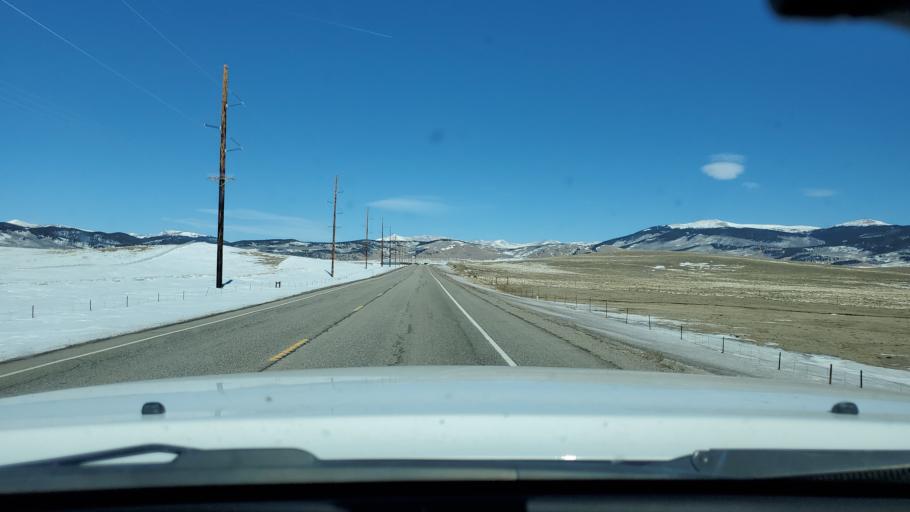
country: US
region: Colorado
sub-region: Park County
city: Fairplay
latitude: 39.3591
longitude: -105.8166
